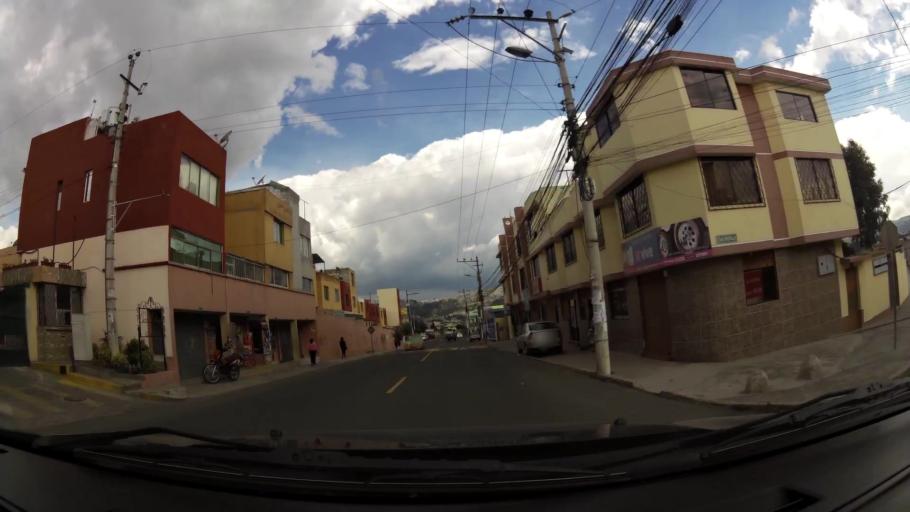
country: EC
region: Pichincha
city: Quito
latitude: -0.0912
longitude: -78.4414
